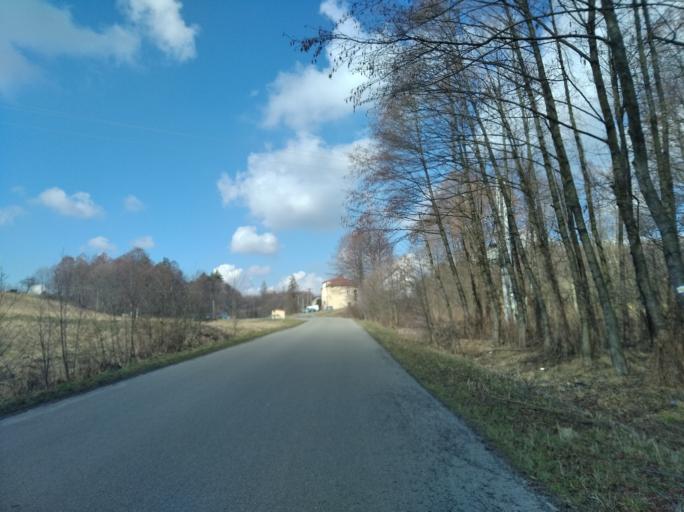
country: PL
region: Subcarpathian Voivodeship
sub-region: Powiat strzyzowski
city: Frysztak
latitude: 49.8726
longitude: 21.5277
